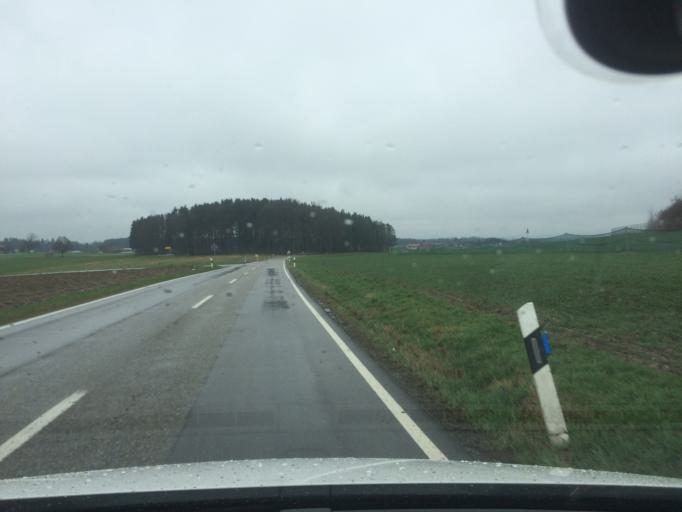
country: DE
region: Bavaria
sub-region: Upper Bavaria
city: Assling
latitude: 47.9597
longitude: 11.9685
